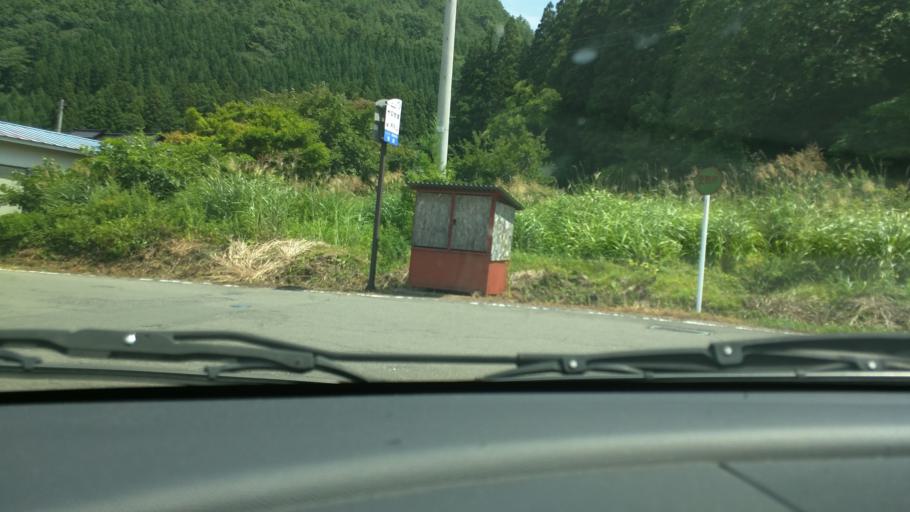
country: JP
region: Fukushima
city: Inawashiro
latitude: 37.3794
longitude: 140.0670
